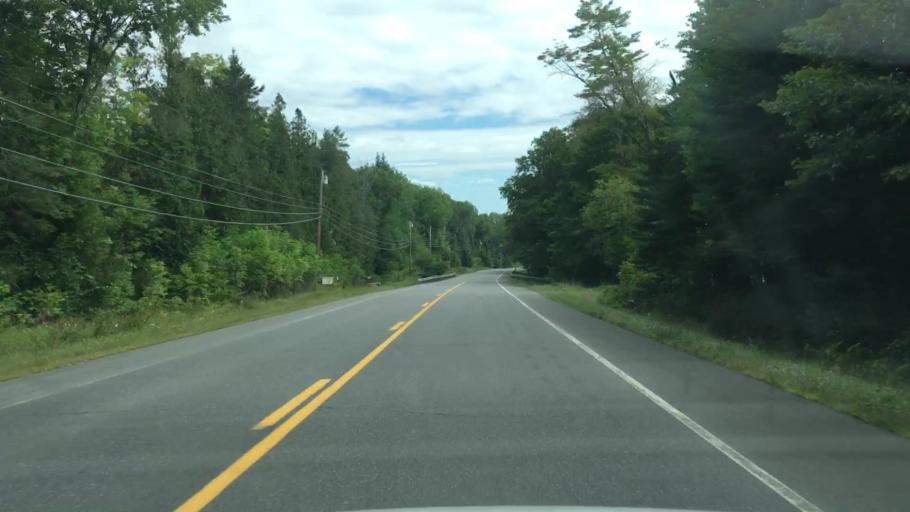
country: US
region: Maine
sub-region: Piscataquis County
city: Dover-Foxcroft
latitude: 45.2262
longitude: -69.1191
